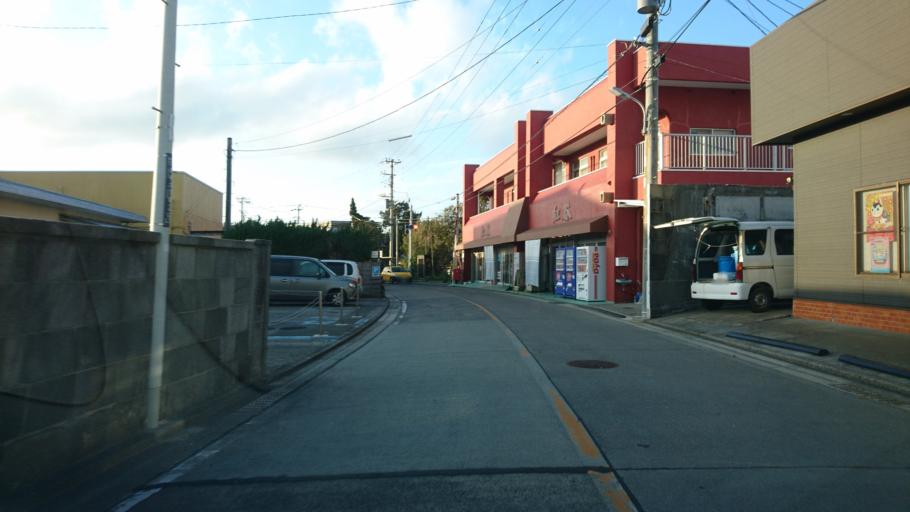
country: JP
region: Shizuoka
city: Shimoda
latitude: 34.3754
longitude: 139.2541
